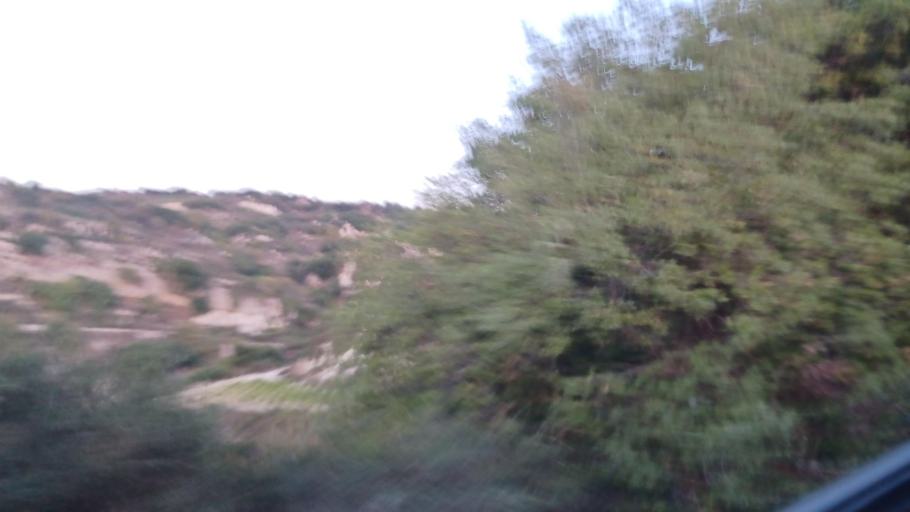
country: CY
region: Pafos
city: Mesogi
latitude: 34.8559
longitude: 32.5024
